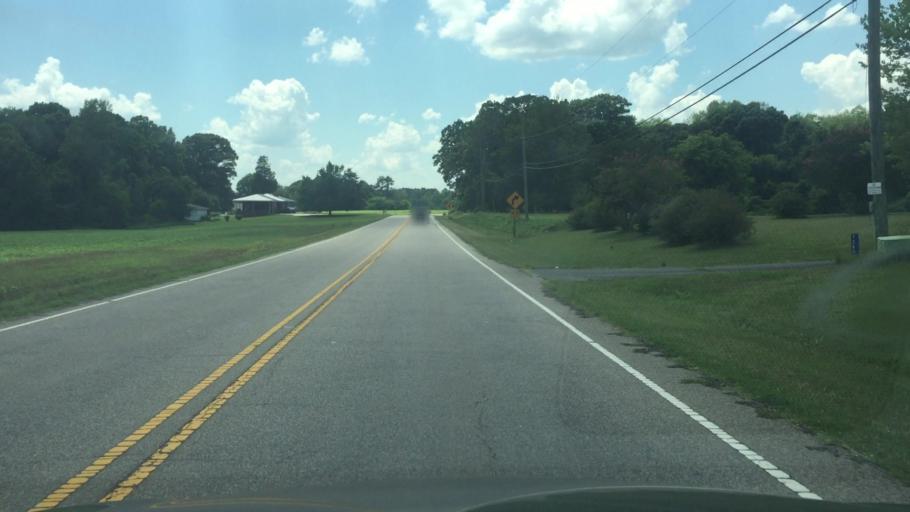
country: US
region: North Carolina
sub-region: Rowan County
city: Enochville
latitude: 35.5766
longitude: -80.7055
